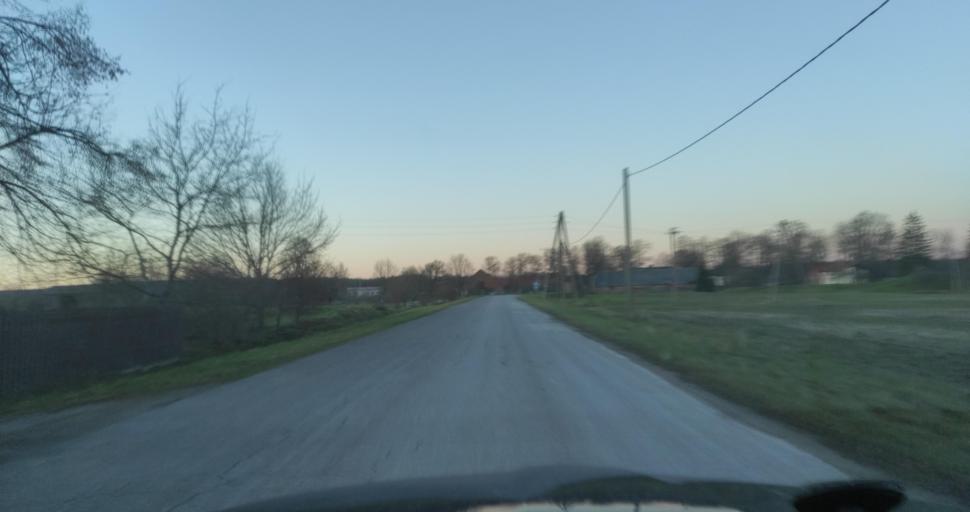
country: LV
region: Dundaga
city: Dundaga
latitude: 57.3735
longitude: 22.2315
